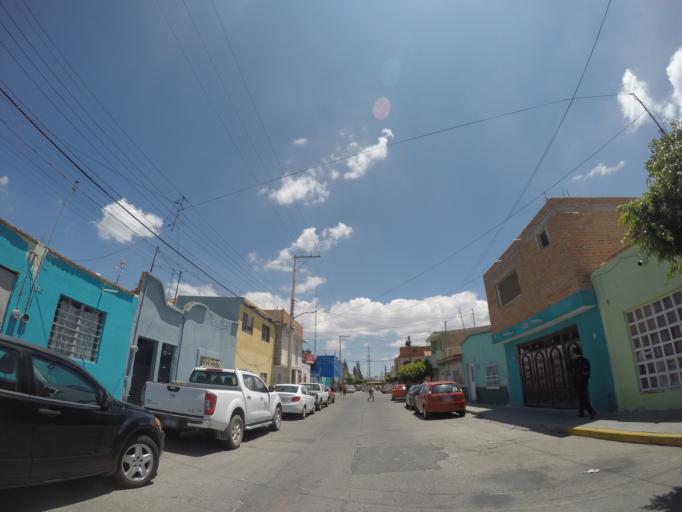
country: MX
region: San Luis Potosi
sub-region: San Luis Potosi
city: San Luis Potosi
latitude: 22.1535
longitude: -100.9599
